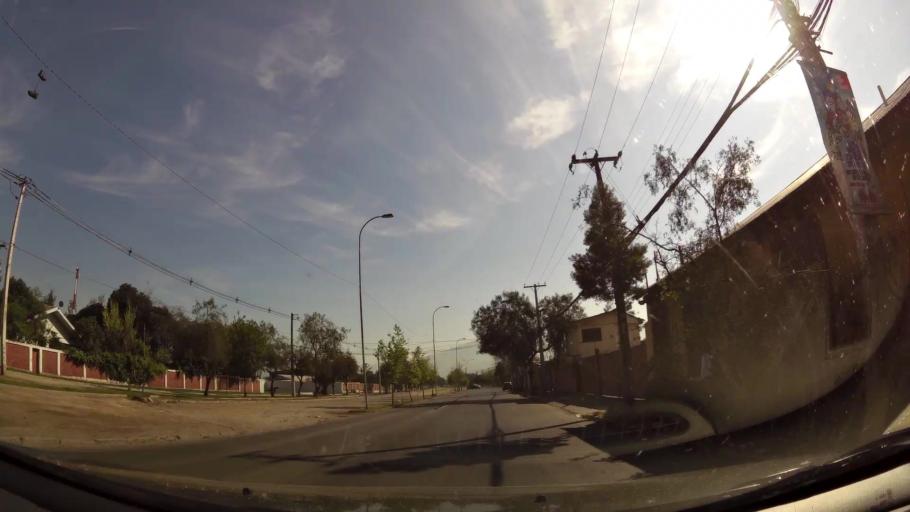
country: CL
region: Santiago Metropolitan
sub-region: Provincia de Santiago
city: Santiago
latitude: -33.3997
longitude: -70.6582
